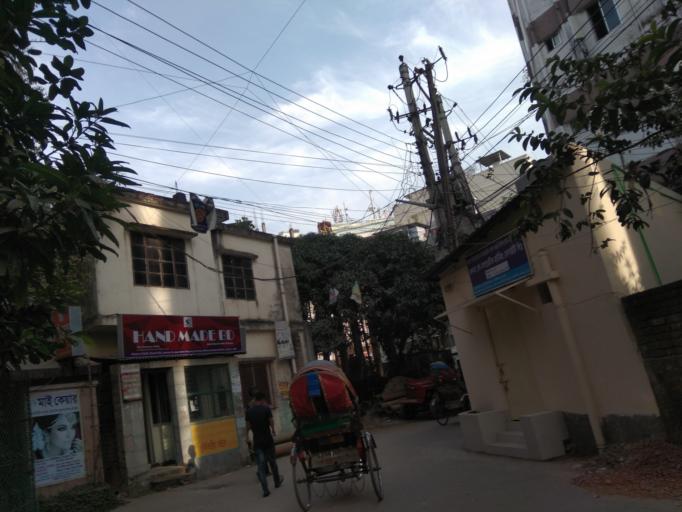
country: BD
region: Dhaka
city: Azimpur
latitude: 23.7701
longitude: 90.3576
